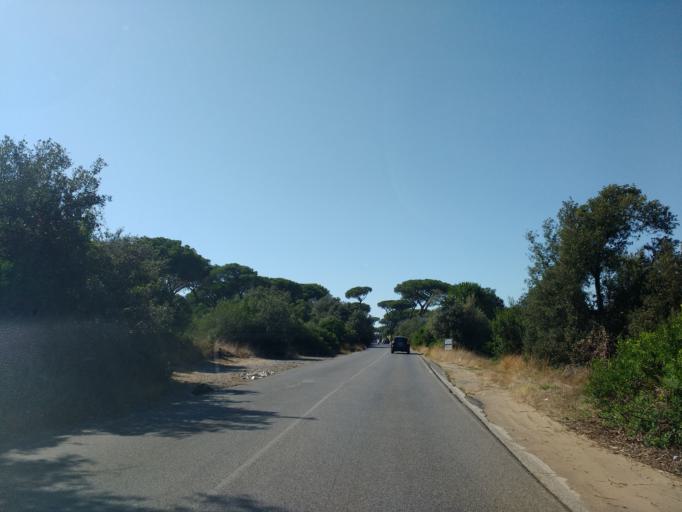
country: IT
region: Latium
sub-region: Citta metropolitana di Roma Capitale
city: Acilia-Castel Fusano-Ostia Antica
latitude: 41.7182
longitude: 12.3508
